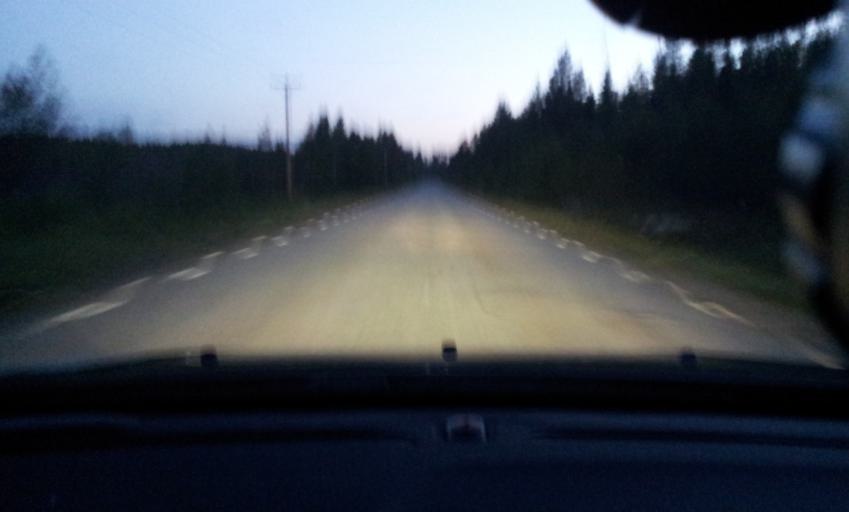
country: SE
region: Jaemtland
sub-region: Bergs Kommun
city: Hoverberg
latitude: 62.6815
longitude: 14.6553
